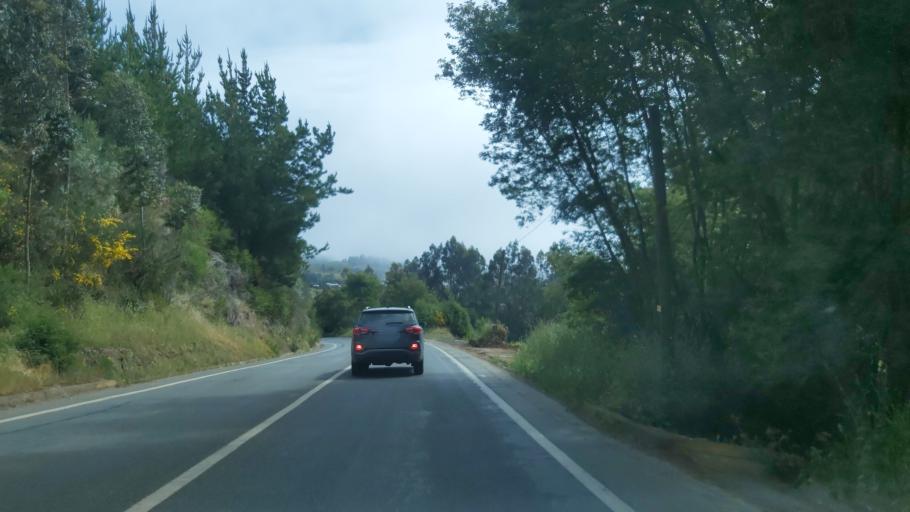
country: CL
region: Maule
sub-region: Provincia de Cauquenes
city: Cauquenes
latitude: -35.8686
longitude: -72.6541
